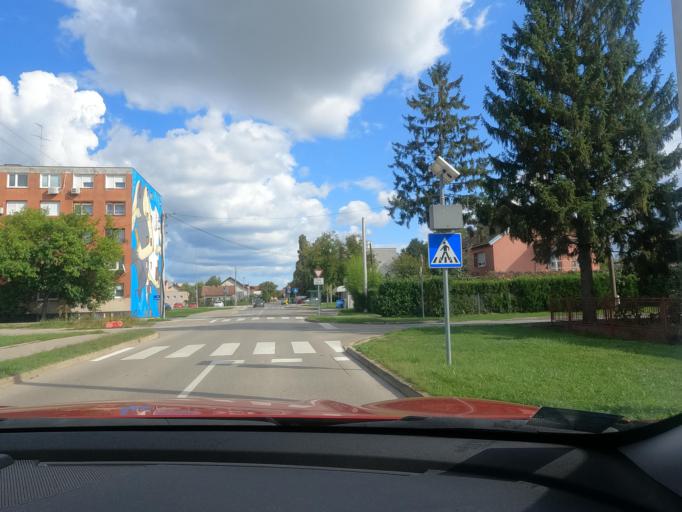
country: HR
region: Sisacko-Moslavacka
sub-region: Grad Sisak
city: Sisak
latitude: 45.4990
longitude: 16.3687
